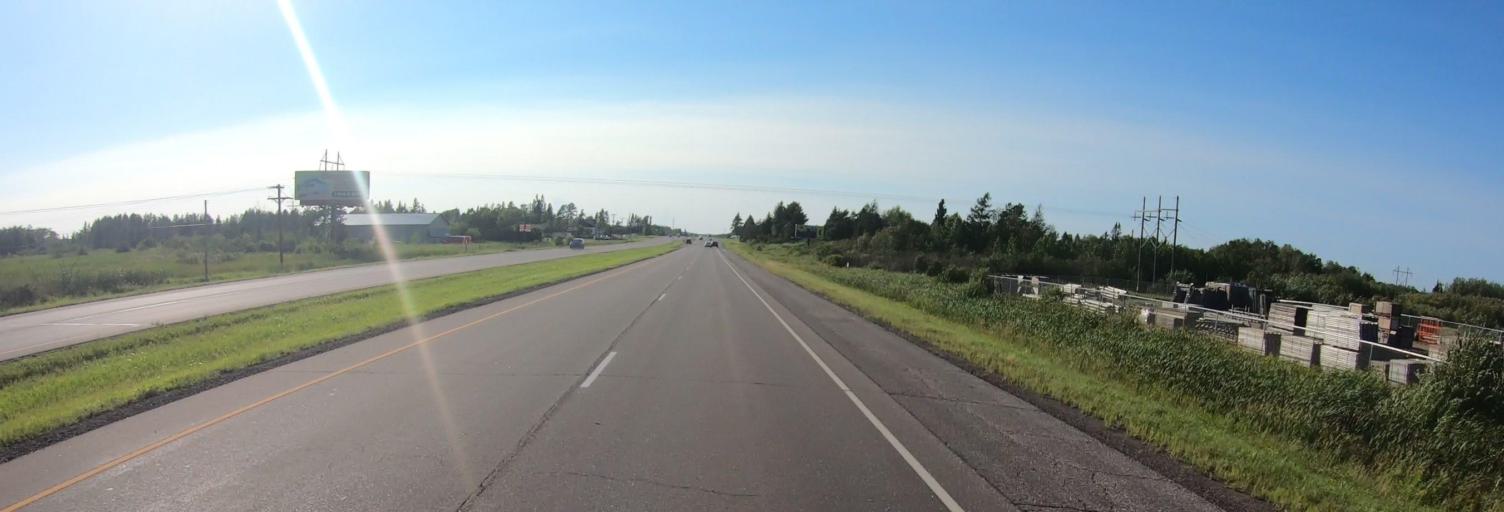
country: US
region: Minnesota
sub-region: Saint Louis County
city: Hermantown
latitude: 46.8376
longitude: -92.2427
